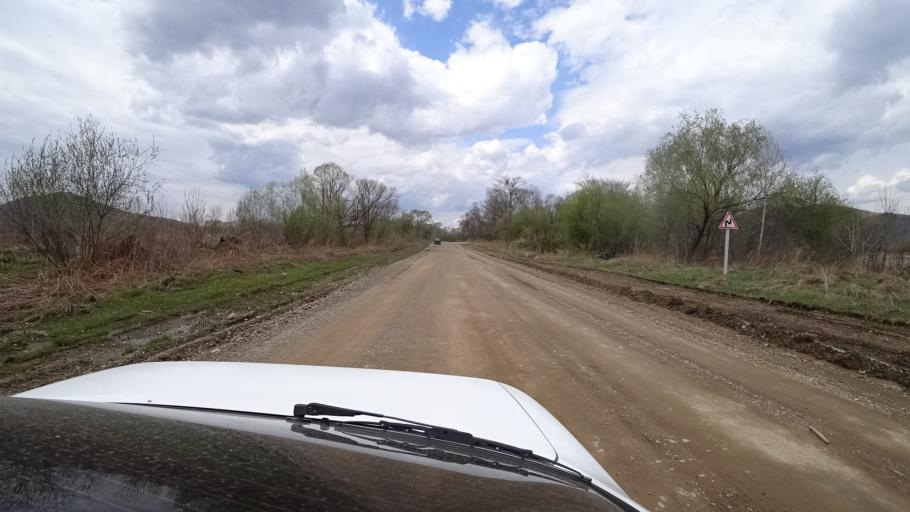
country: RU
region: Primorskiy
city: Novopokrovka
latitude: 45.6100
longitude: 134.2757
